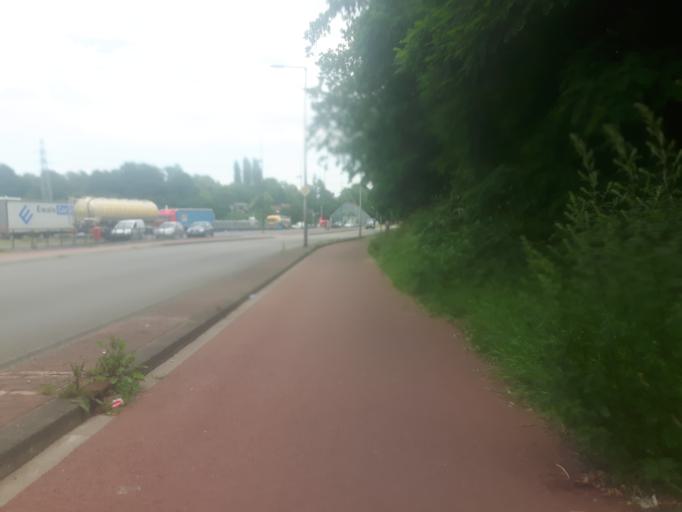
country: NL
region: Overijssel
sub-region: Gemeente Enschede
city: Enschede
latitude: 52.2209
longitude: 6.8591
